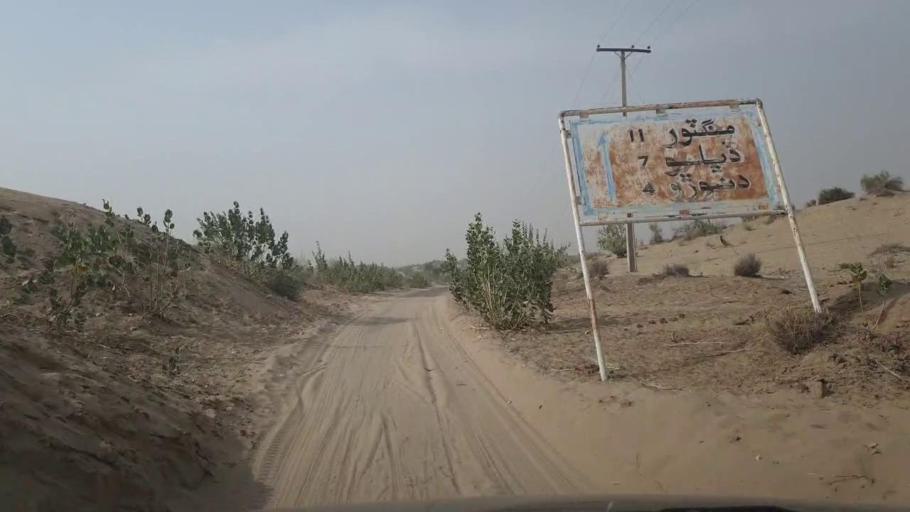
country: PK
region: Sindh
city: Chor
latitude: 25.5920
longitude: 69.9478
